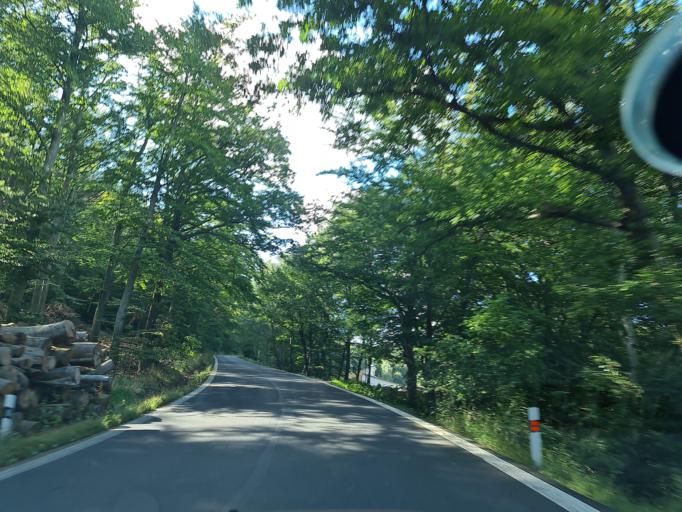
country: CZ
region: Ustecky
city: Mezibori
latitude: 50.6089
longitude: 13.5816
